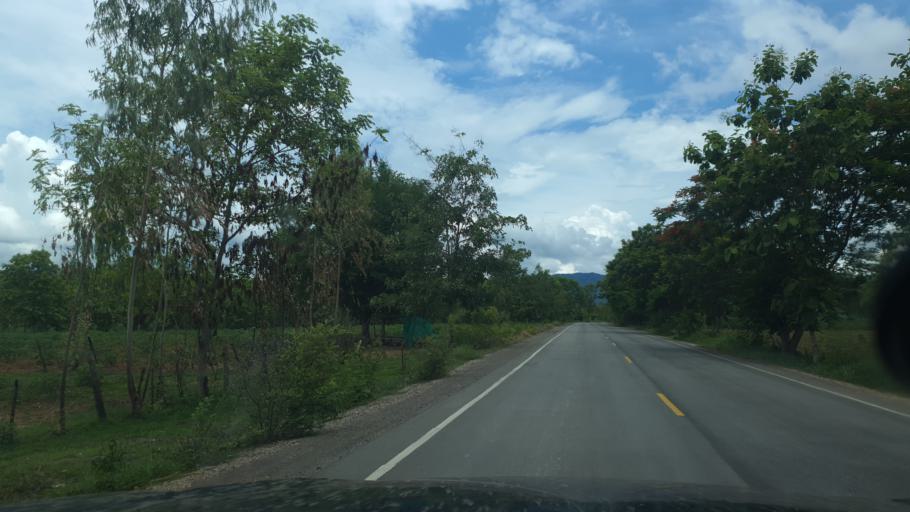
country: TH
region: Lampang
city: Sop Prap
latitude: 17.9242
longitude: 99.3817
